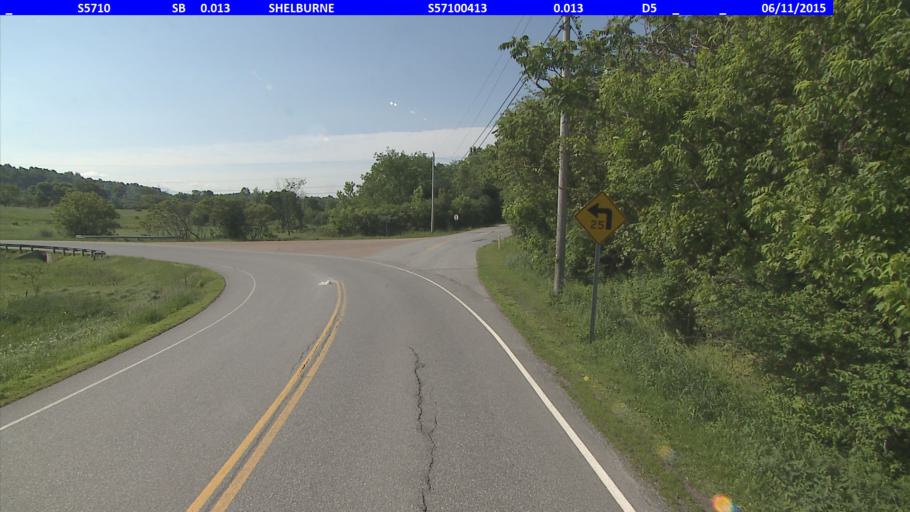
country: US
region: Vermont
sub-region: Chittenden County
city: Hinesburg
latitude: 44.3654
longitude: -73.1790
